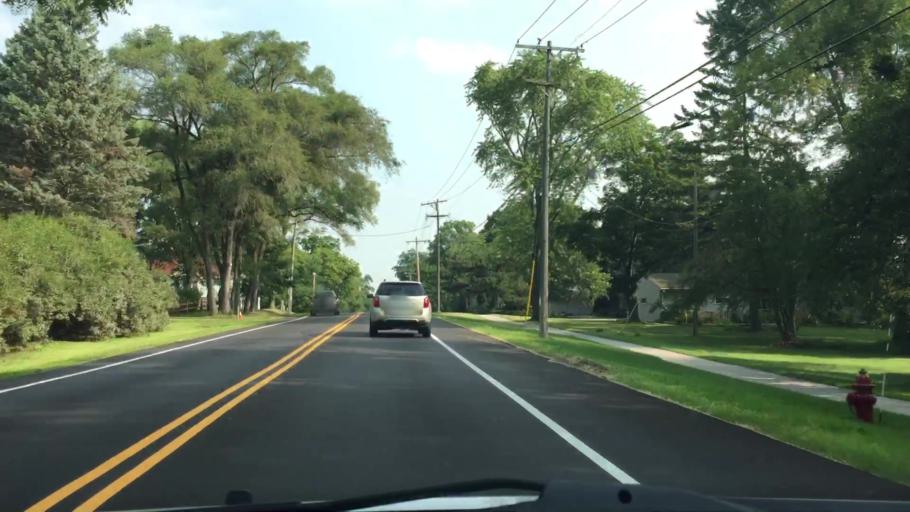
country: US
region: Wisconsin
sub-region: Waukesha County
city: Brookfield
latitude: 43.0669
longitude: -88.1459
